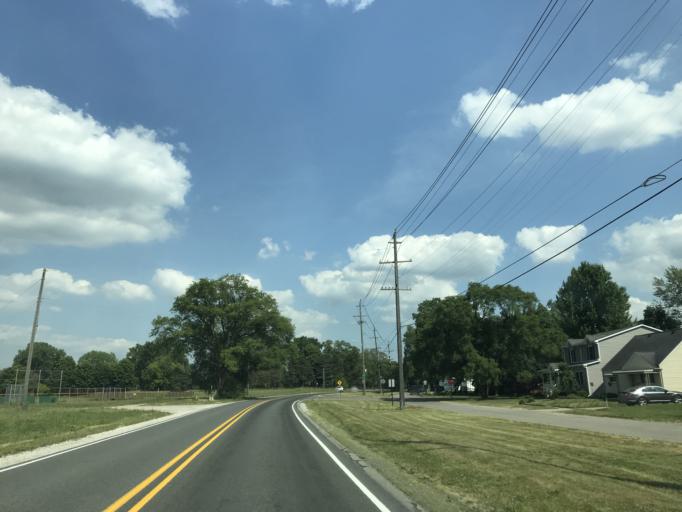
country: US
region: Michigan
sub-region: Washtenaw County
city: Ypsilanti
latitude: 42.2603
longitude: -83.5856
